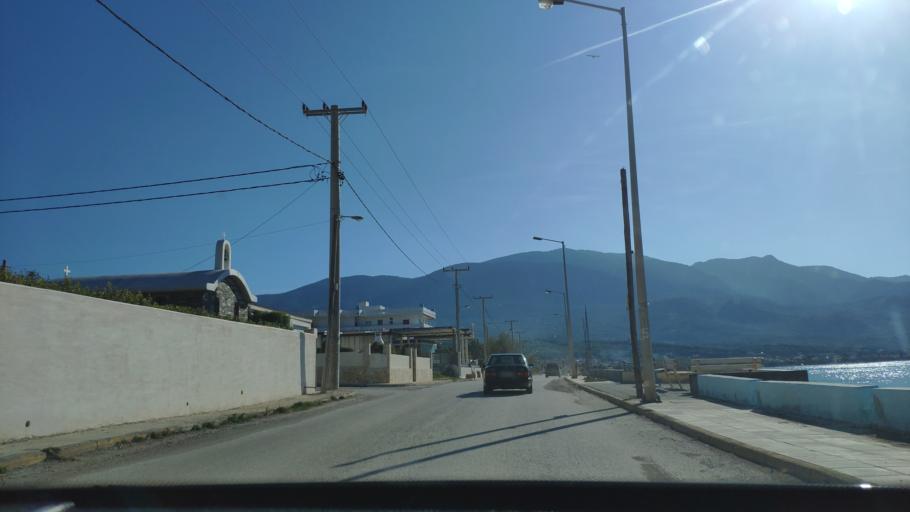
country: GR
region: Attica
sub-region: Nomarchia Dytikis Attikis
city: Kineta
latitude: 38.0816
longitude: 23.1767
